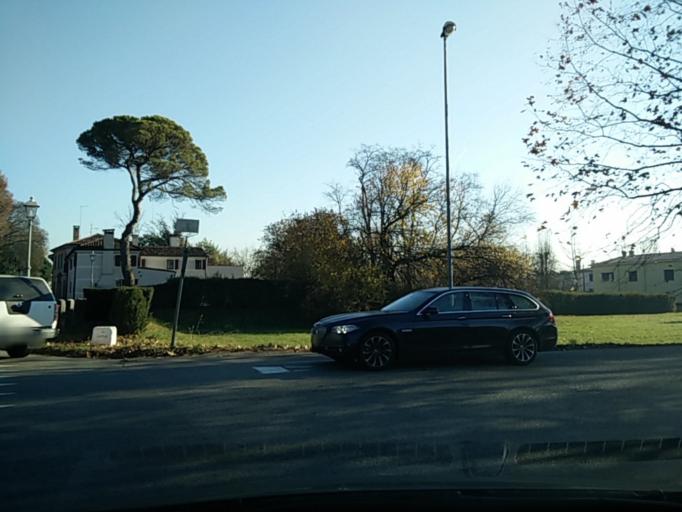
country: IT
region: Veneto
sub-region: Provincia di Treviso
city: Carbonera
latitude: 45.6770
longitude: 12.2840
